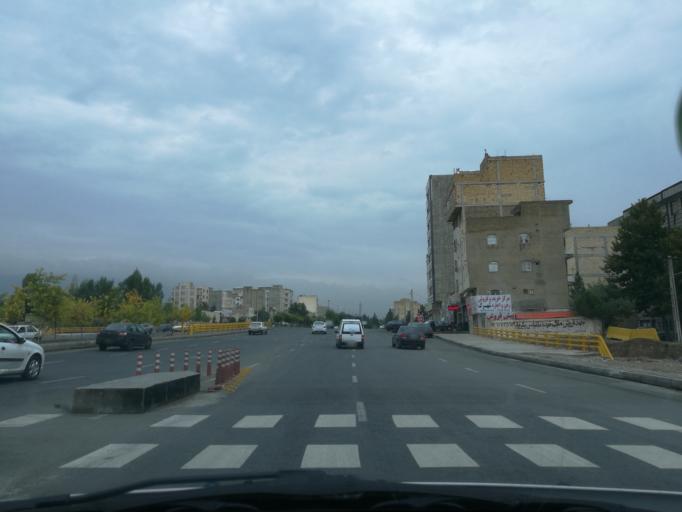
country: IR
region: Alborz
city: Karaj
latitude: 35.8618
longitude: 50.9366
